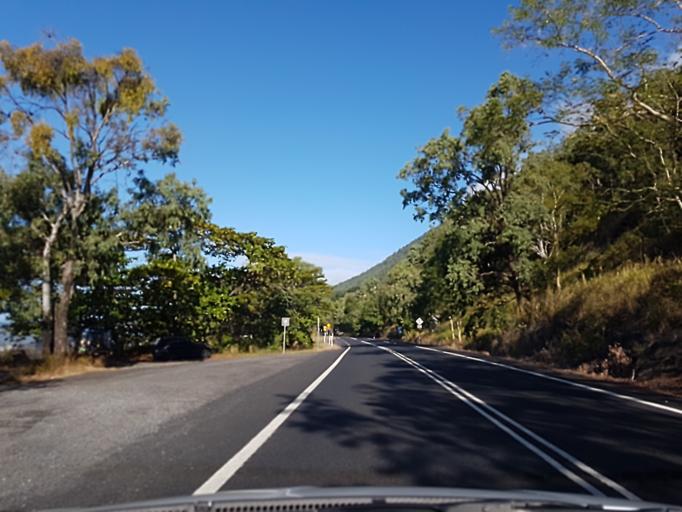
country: AU
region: Queensland
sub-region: Cairns
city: Palm Cove
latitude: -16.7211
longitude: 145.6416
